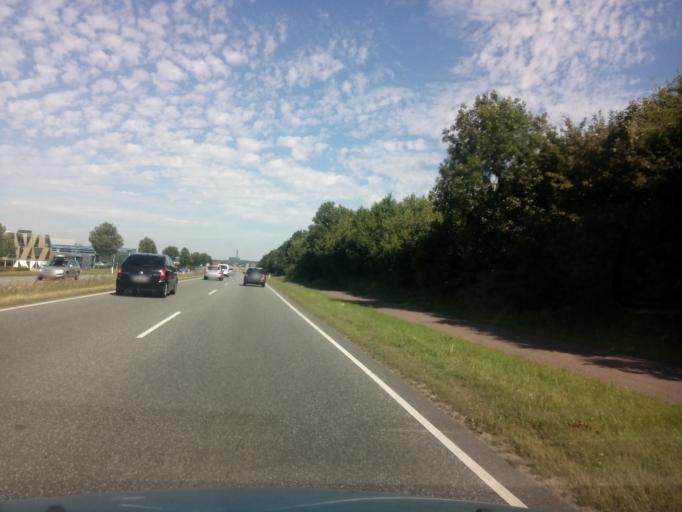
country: DK
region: Central Jutland
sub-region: Arhus Kommune
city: Arhus
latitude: 56.1945
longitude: 10.1862
